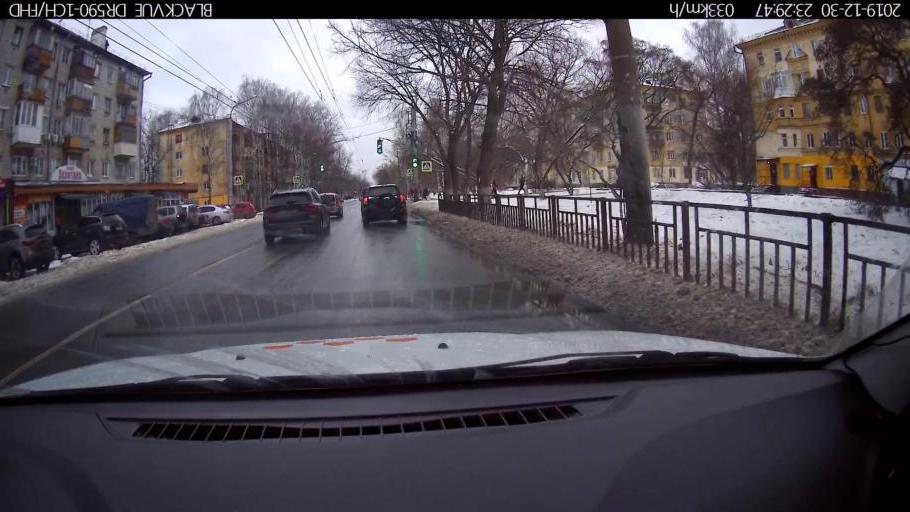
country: RU
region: Nizjnij Novgorod
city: Nizhniy Novgorod
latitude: 56.2820
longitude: 43.9305
